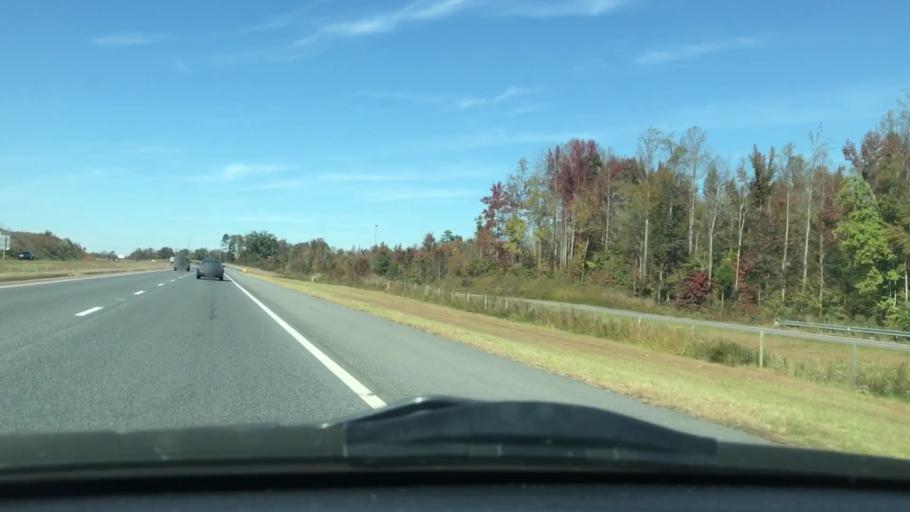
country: US
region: North Carolina
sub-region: Randolph County
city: Randleman
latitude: 35.8381
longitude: -79.8619
